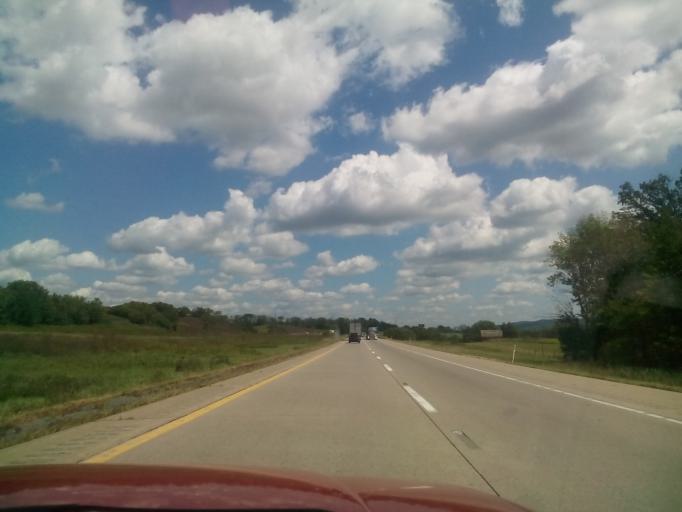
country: US
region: Pennsylvania
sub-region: Northumberland County
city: Riverside
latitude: 40.9882
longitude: -76.6878
